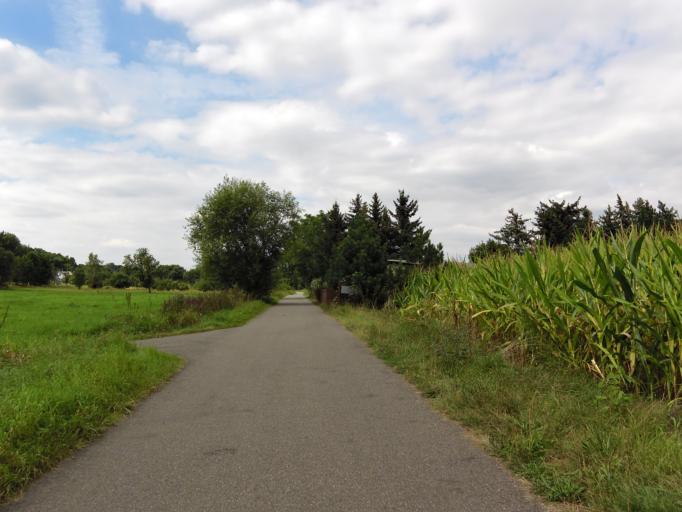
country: DE
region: Saxony
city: Coswig
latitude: 51.1076
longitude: 13.5742
